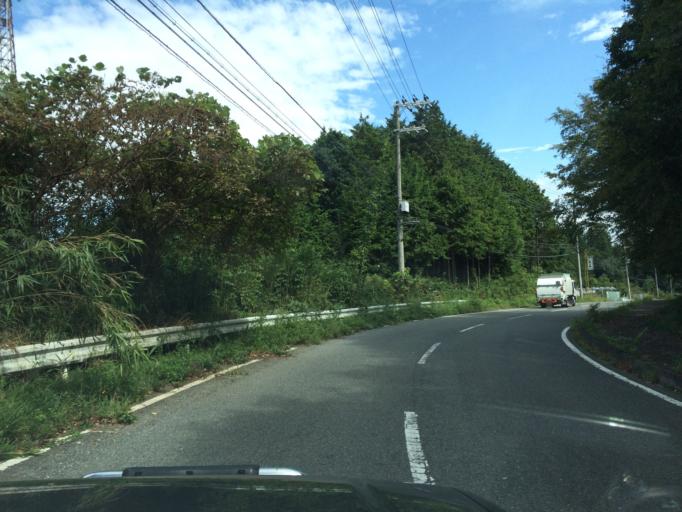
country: JP
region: Mie
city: Nabari
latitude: 34.6815
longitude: 135.9955
